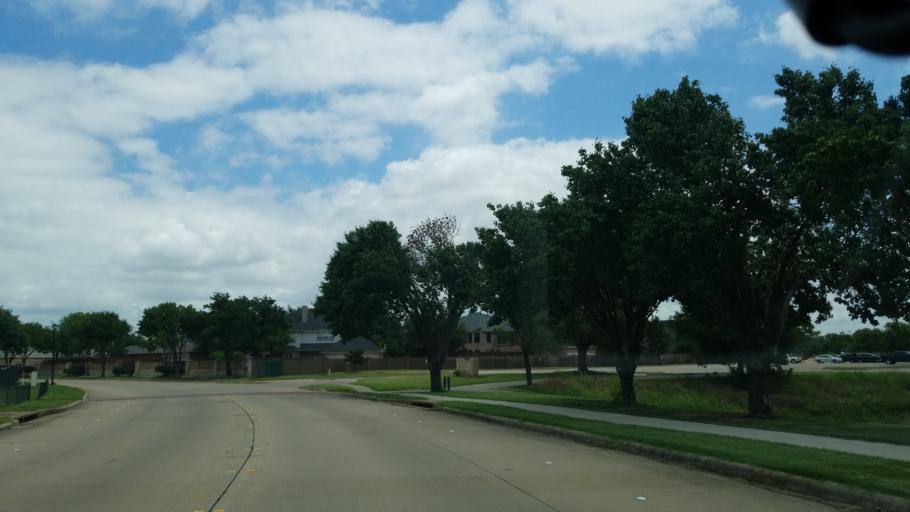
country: US
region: Texas
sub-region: Dallas County
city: Carrollton
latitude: 32.9556
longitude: -96.9479
